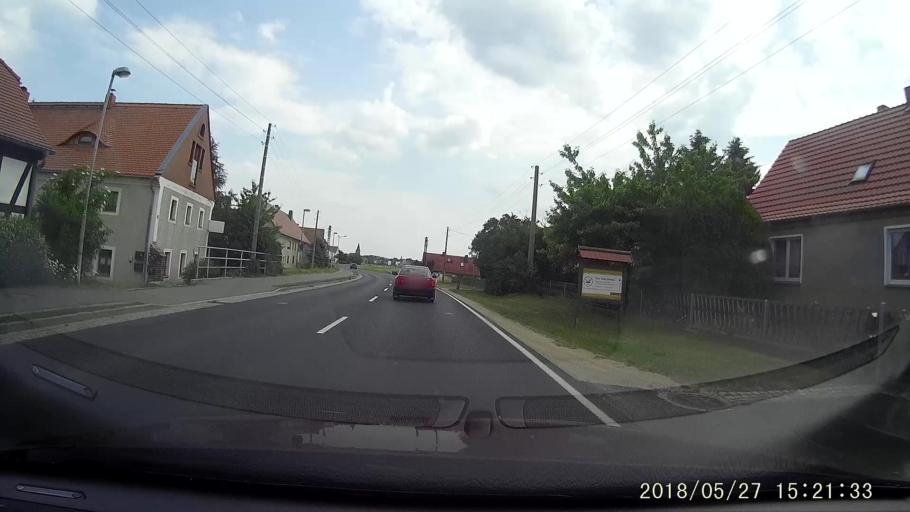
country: DE
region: Saxony
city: Kodersdorf
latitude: 51.2398
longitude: 14.8887
